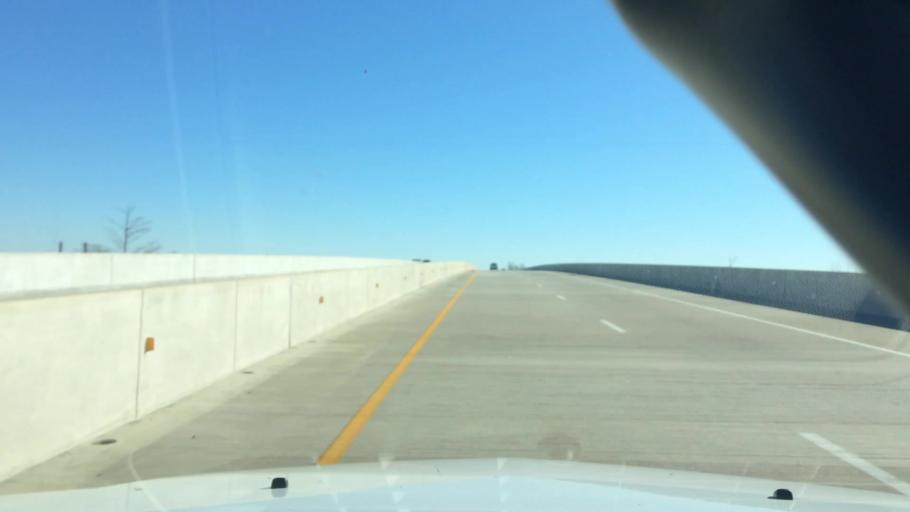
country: US
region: North Carolina
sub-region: Brunswick County
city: Navassa
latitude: 34.2731
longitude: -78.0047
